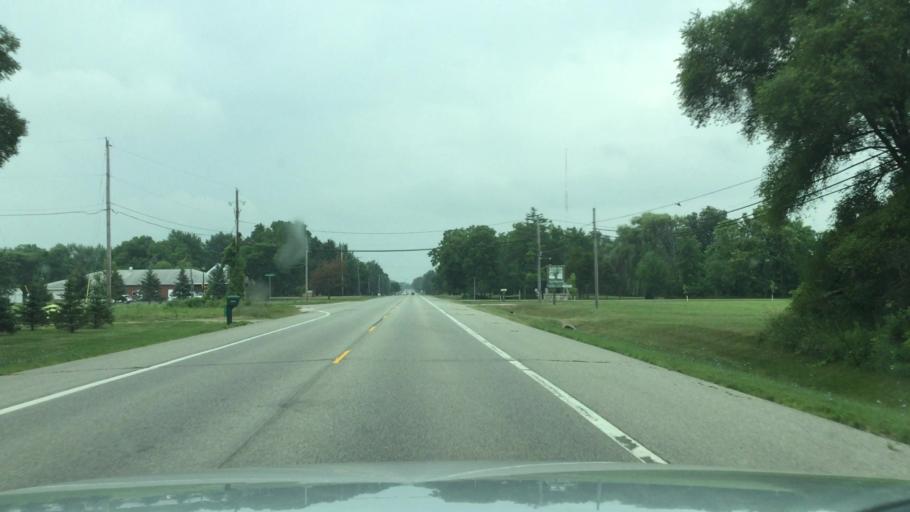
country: US
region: Michigan
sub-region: Shiawassee County
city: Owosso
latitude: 43.0361
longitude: -84.1770
